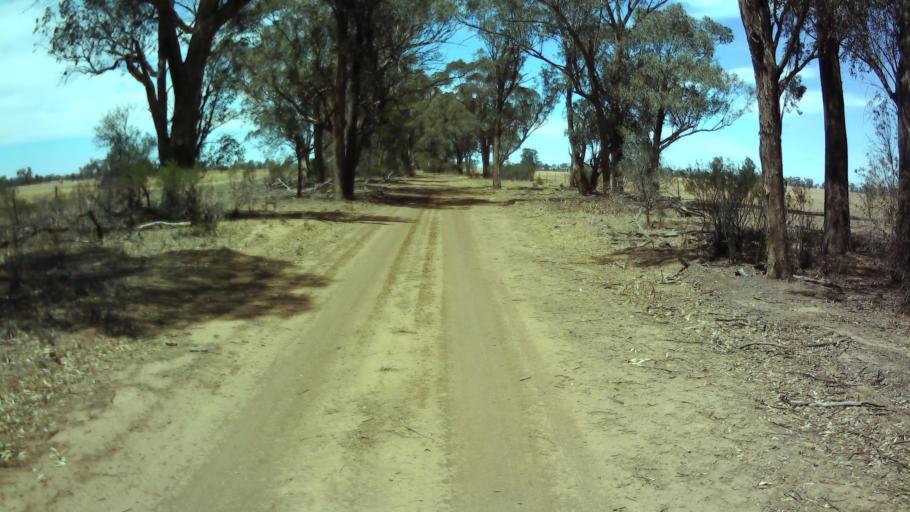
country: AU
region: New South Wales
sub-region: Weddin
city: Grenfell
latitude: -33.9159
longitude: 147.8056
